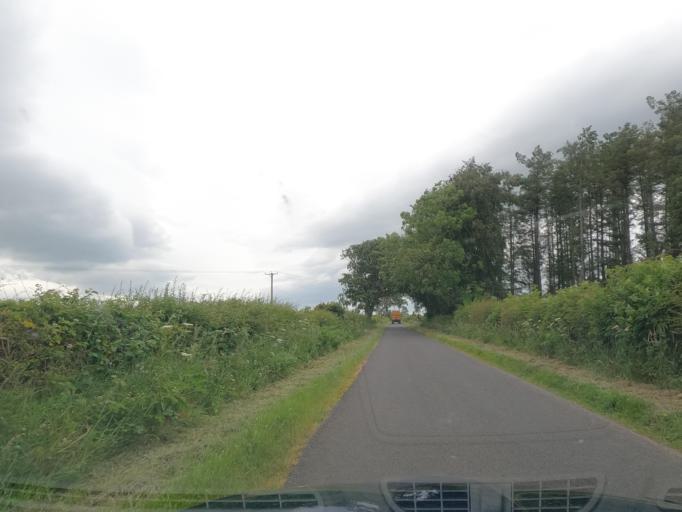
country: GB
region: England
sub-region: Northumberland
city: Lowick
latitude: 55.5682
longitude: -1.9126
